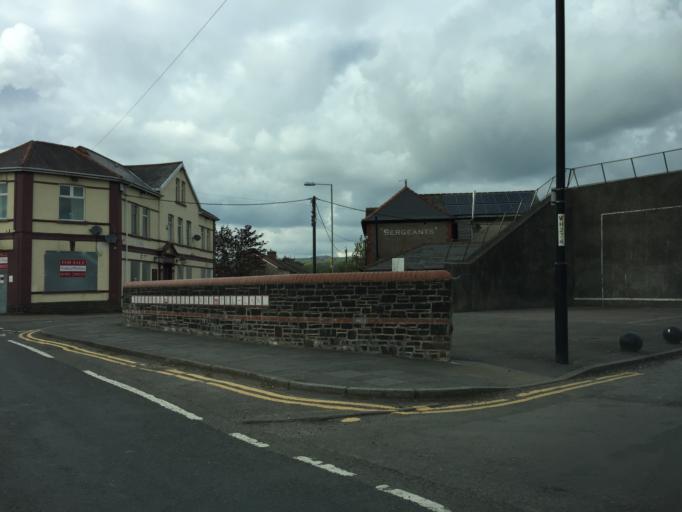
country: GB
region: Wales
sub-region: Caerphilly County Borough
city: Nelson
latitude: 51.6523
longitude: -3.2836
